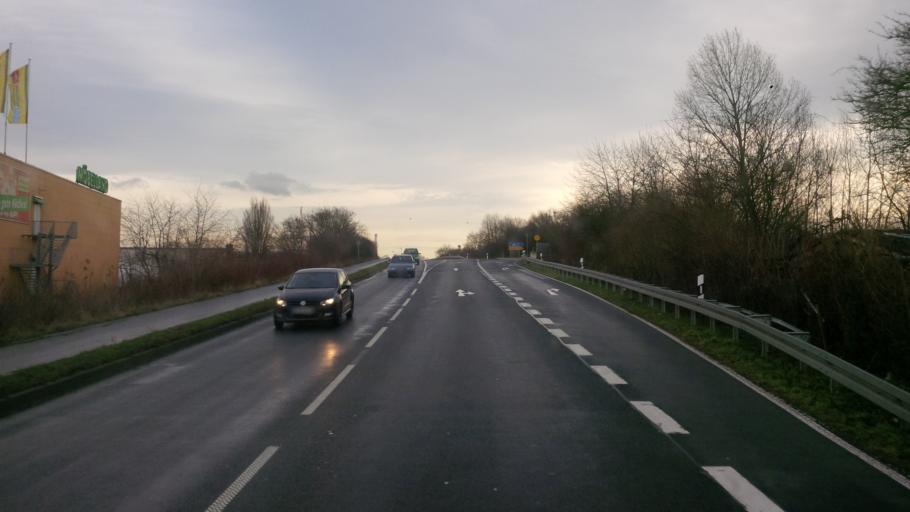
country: DE
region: Hesse
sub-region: Regierungsbezirk Darmstadt
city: Bad Homburg vor der Hoehe
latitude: 50.2160
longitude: 8.6040
